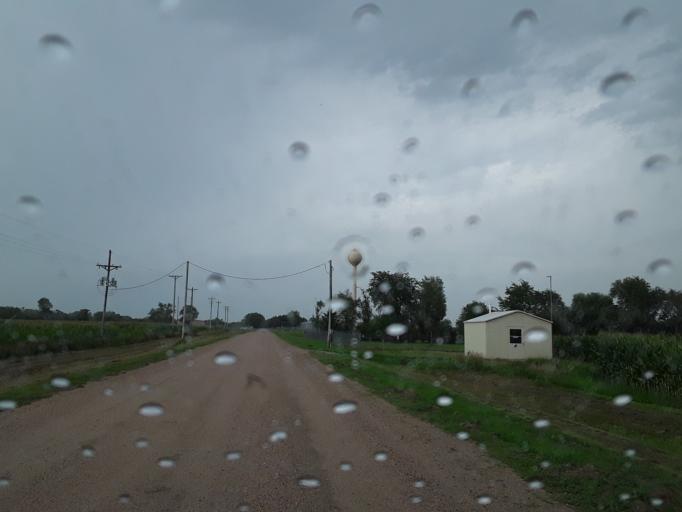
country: US
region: Nebraska
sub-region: Saunders County
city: Yutan
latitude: 41.1822
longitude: -96.4449
